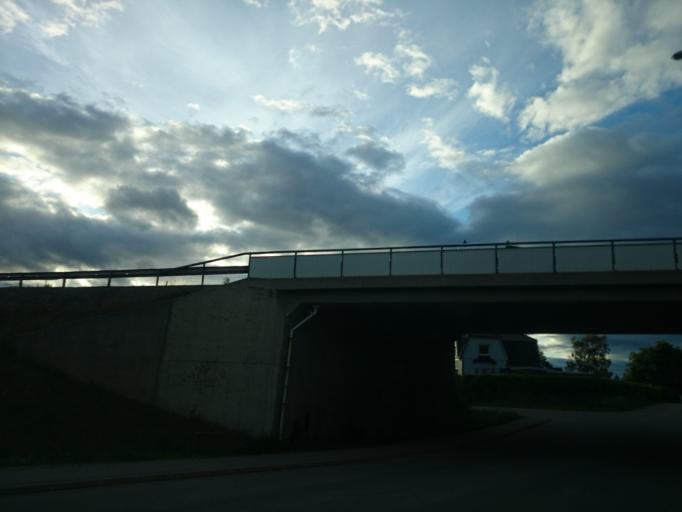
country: SE
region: Vaesternorrland
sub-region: Timra Kommun
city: Bergeforsen
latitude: 62.5151
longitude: 17.3812
